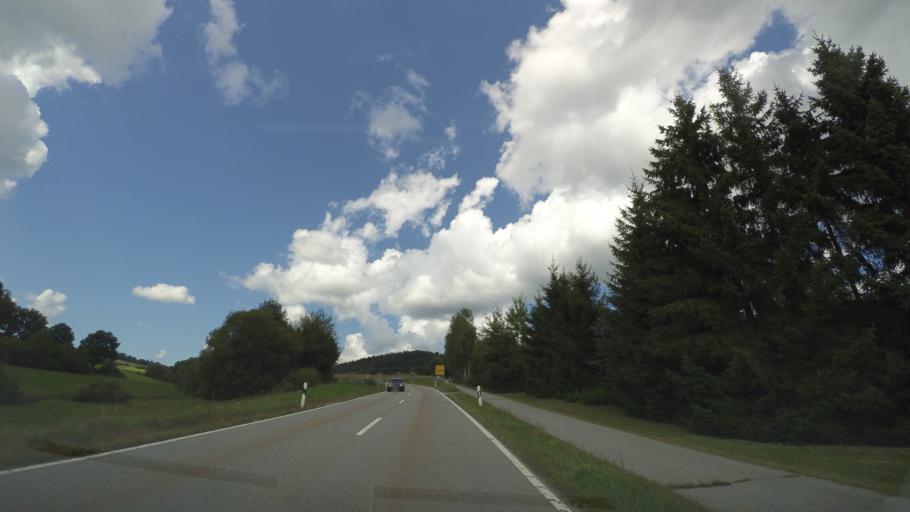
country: DE
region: Bavaria
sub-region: Lower Bavaria
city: Geiersthal
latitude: 49.0515
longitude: 12.9734
